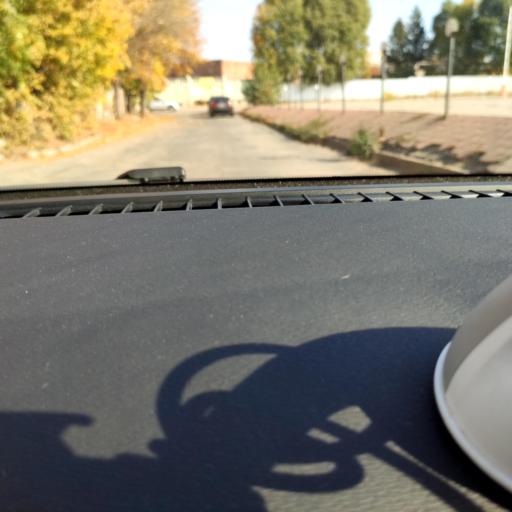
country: RU
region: Samara
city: Samara
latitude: 53.2091
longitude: 50.1841
